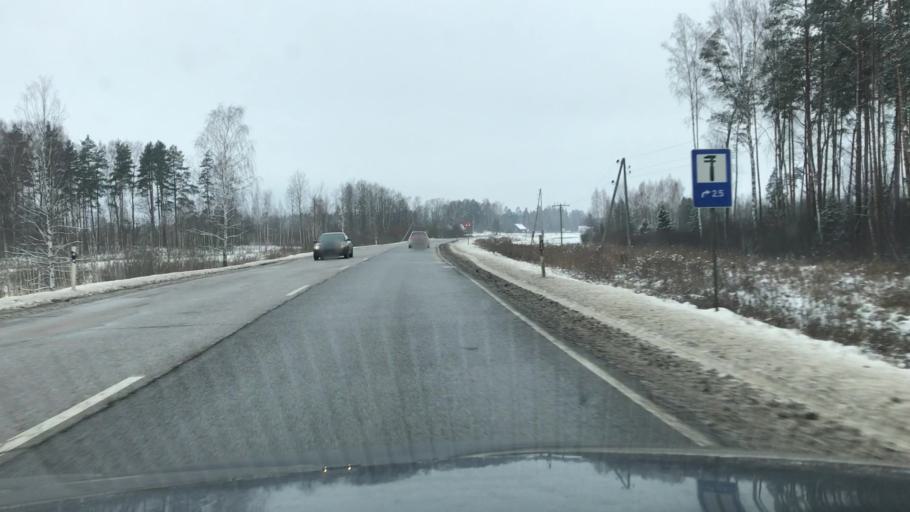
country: LV
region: Baldone
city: Baldone
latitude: 56.7639
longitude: 24.3136
